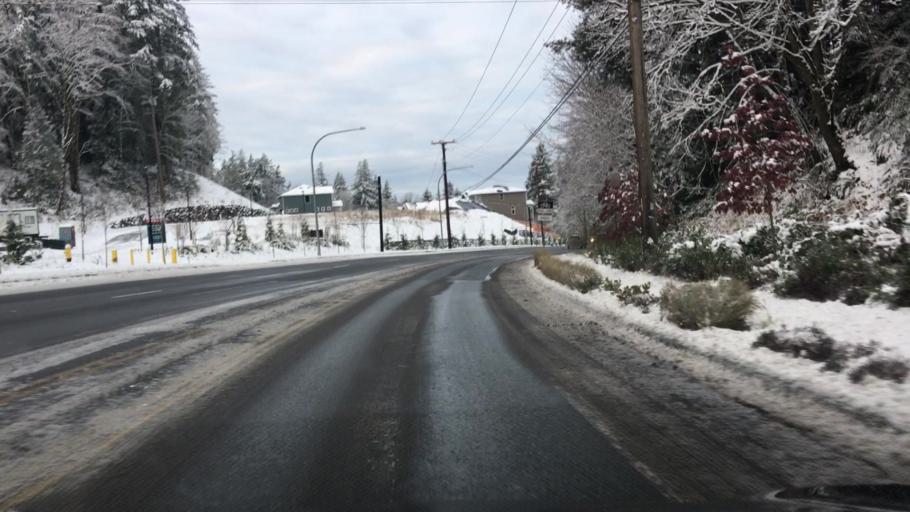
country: US
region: Washington
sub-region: King County
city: Woodinville
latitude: 47.7617
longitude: -122.1335
